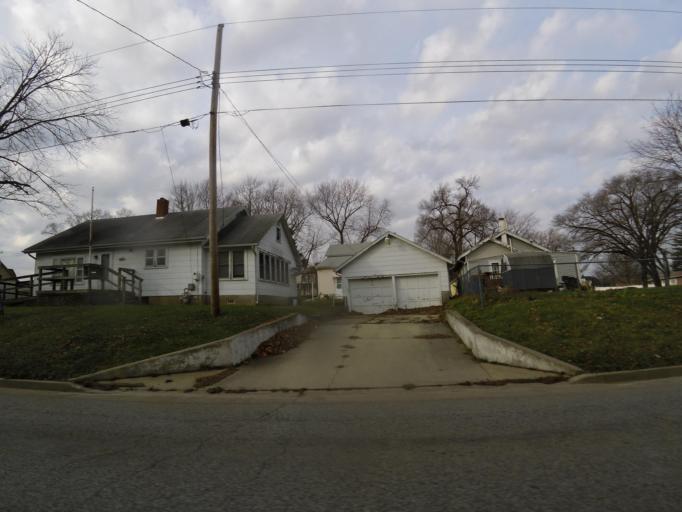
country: US
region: Illinois
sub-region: Christian County
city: Pana
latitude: 39.3817
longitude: -89.0816
